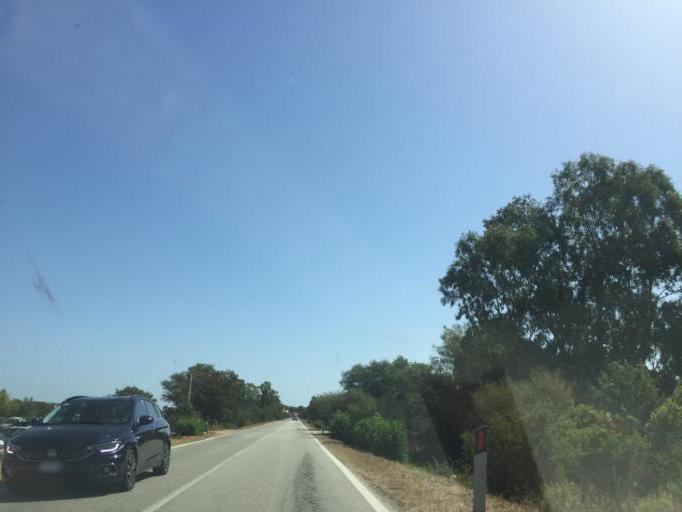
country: IT
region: Sardinia
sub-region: Provincia di Olbia-Tempio
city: San Teodoro
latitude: 40.7613
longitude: 9.6598
